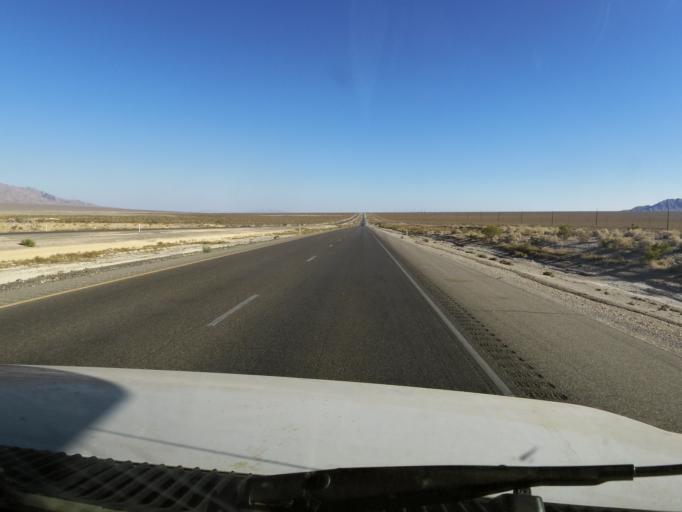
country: US
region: Nevada
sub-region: Clark County
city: Summerlin South
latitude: 36.4138
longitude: -115.4140
